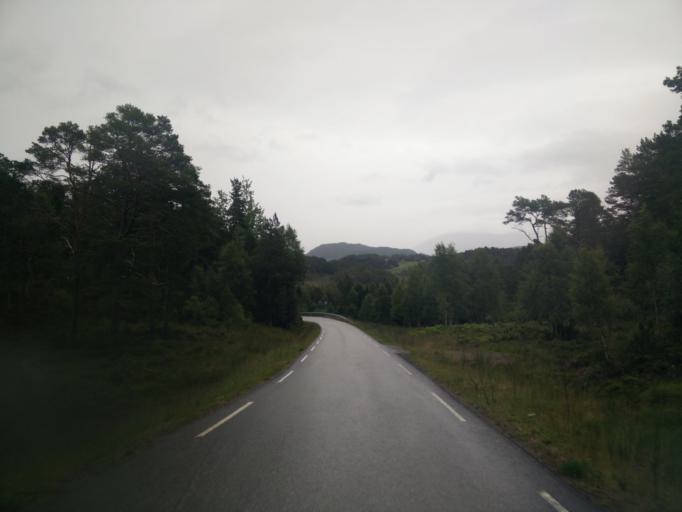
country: NO
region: More og Romsdal
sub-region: Kristiansund
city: Rensvik
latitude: 63.0388
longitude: 7.9294
